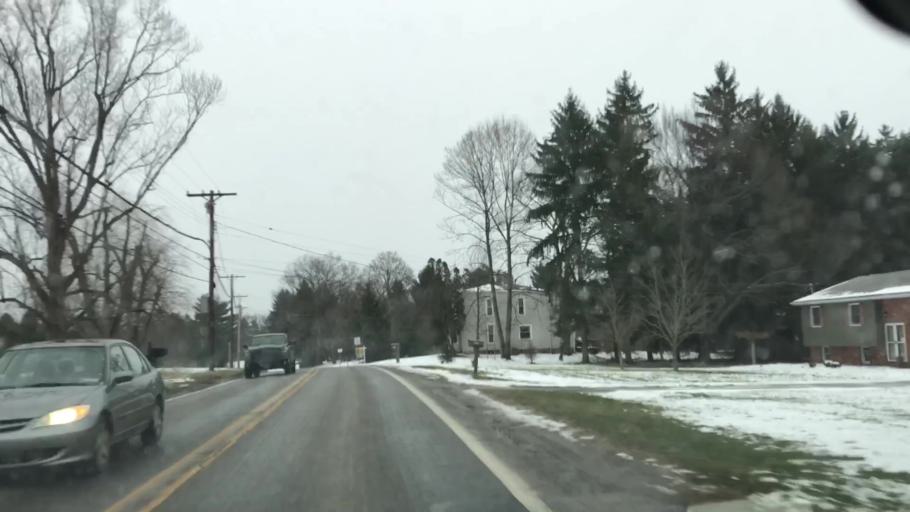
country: US
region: Pennsylvania
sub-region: Beaver County
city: Industry
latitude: 40.6980
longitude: -80.3911
